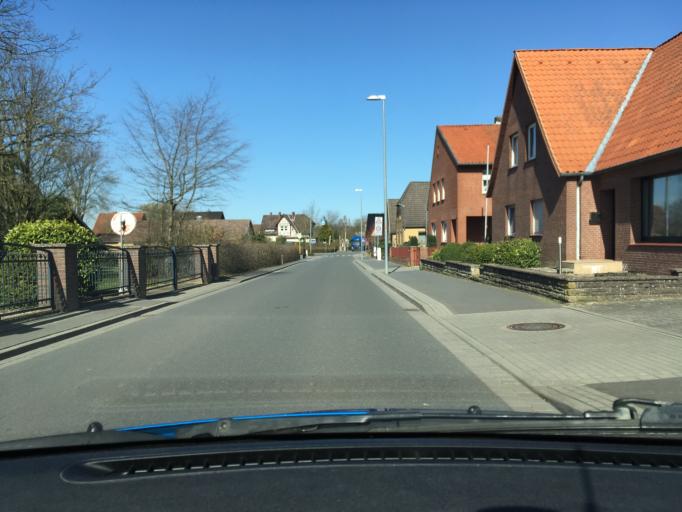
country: DE
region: Lower Saxony
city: Barum
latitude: 52.9950
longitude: 10.5085
